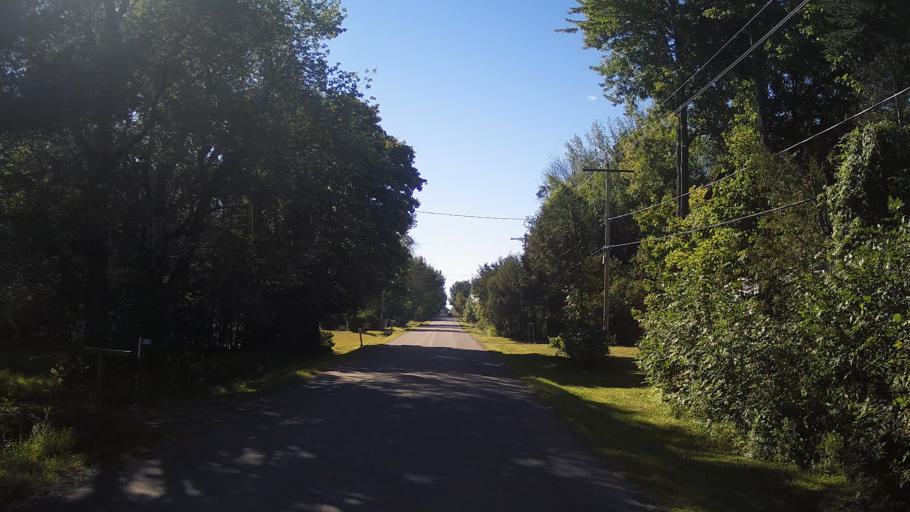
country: CA
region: Ontario
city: Prescott
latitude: 45.0138
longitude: -75.6118
